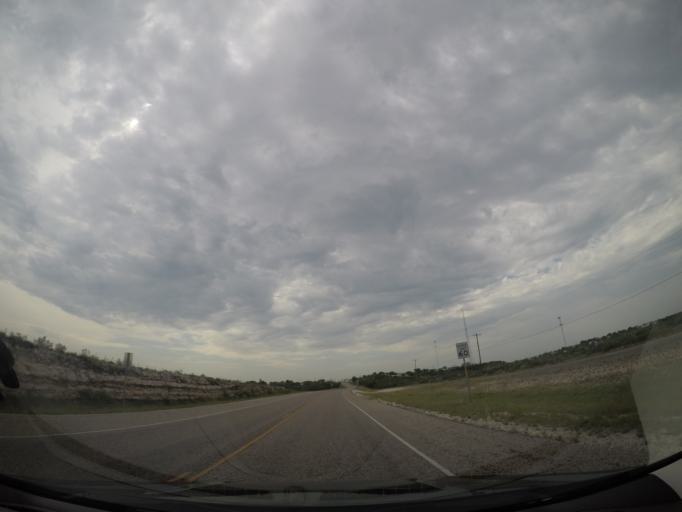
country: US
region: Texas
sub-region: Val Verde County
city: Cienegas Terrace
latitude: 29.6907
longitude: -101.1789
